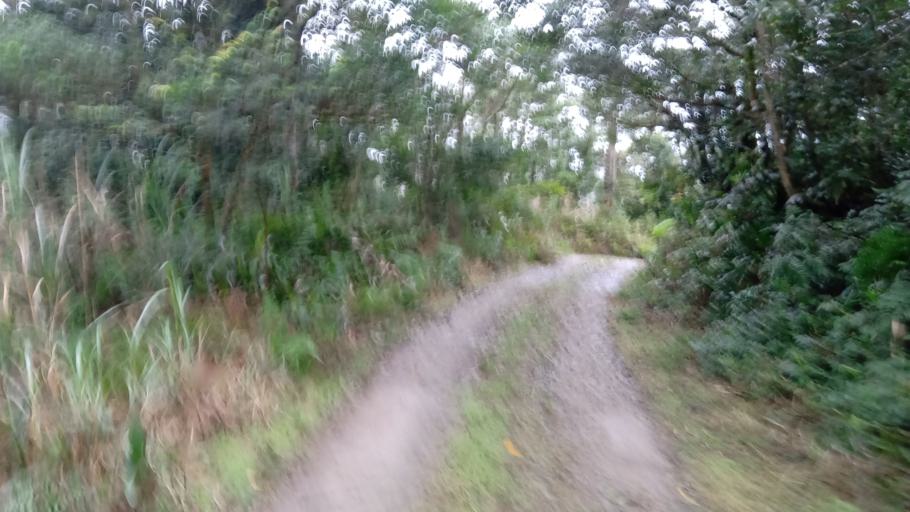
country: TW
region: Taiwan
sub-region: Yilan
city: Yilan
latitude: 24.8167
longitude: 121.6900
